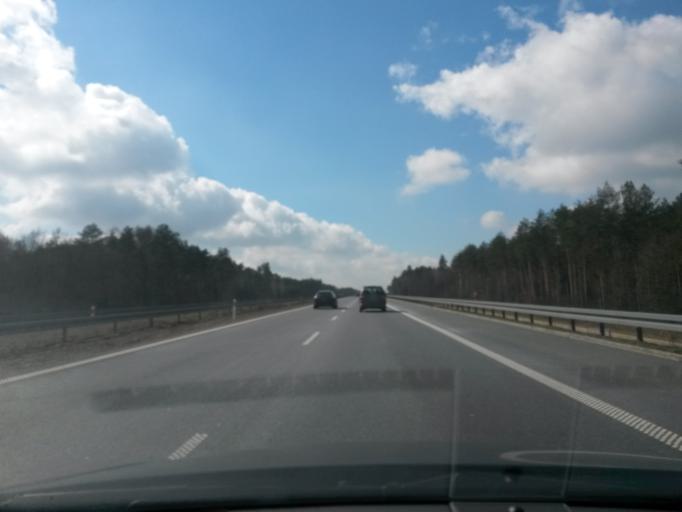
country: PL
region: Lodz Voivodeship
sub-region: Powiat skierniewicki
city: Bolimow
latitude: 52.0569
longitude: 20.1380
